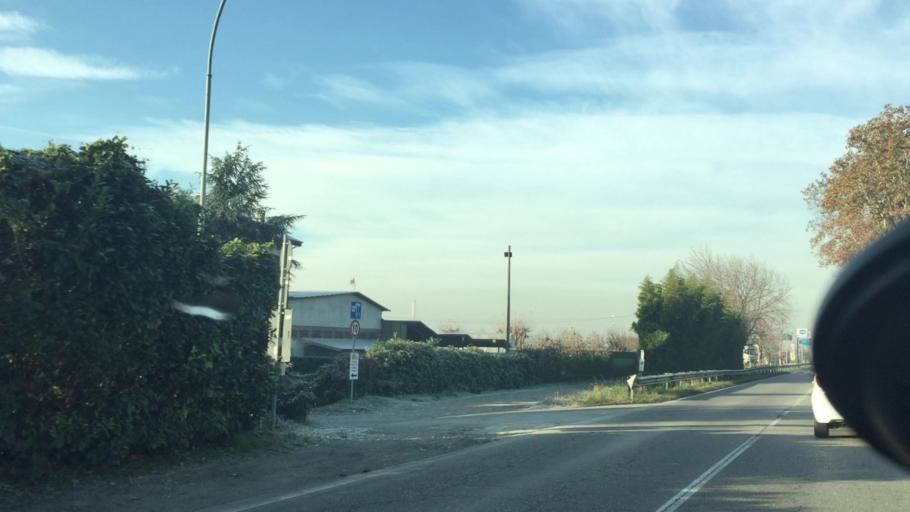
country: IT
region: Lombardy
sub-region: Provincia di Bergamo
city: Badalasco
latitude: 45.5238
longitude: 9.5563
